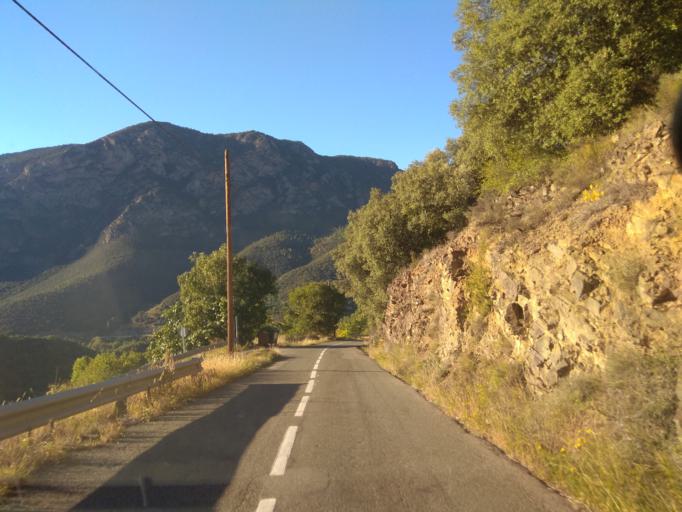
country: ES
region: Catalonia
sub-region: Provincia de Lleida
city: el Pont de Bar
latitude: 42.3533
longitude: 1.5825
